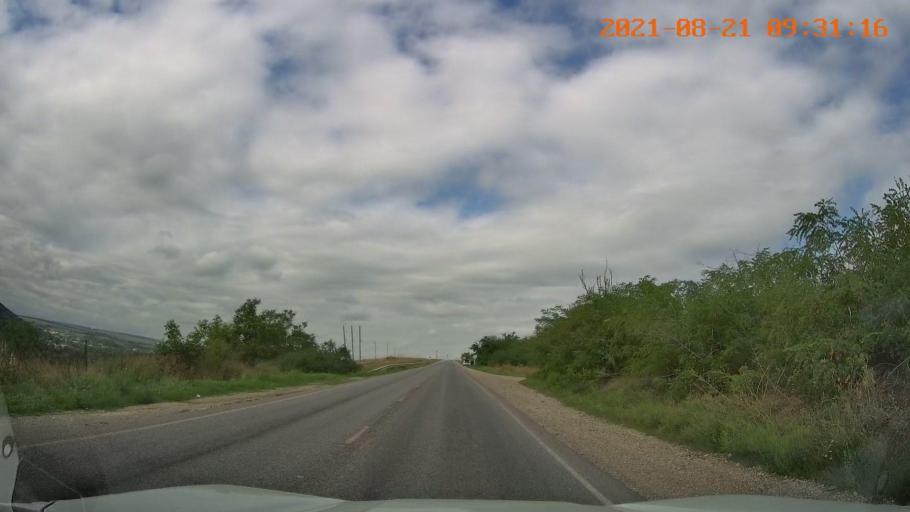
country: RU
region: Stavropol'skiy
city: Yutsa
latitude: 43.9901
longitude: 43.0286
